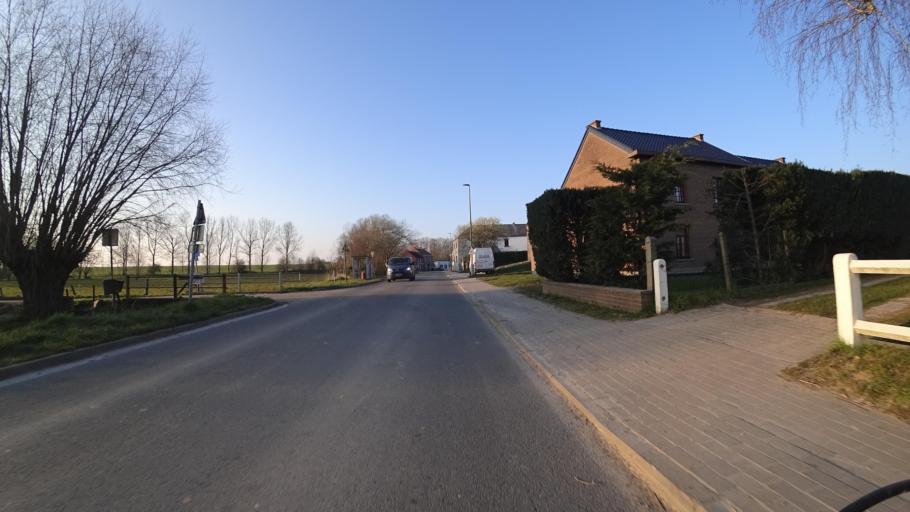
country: BE
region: Wallonia
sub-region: Province du Brabant Wallon
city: Chastre
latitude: 50.5823
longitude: 4.6394
